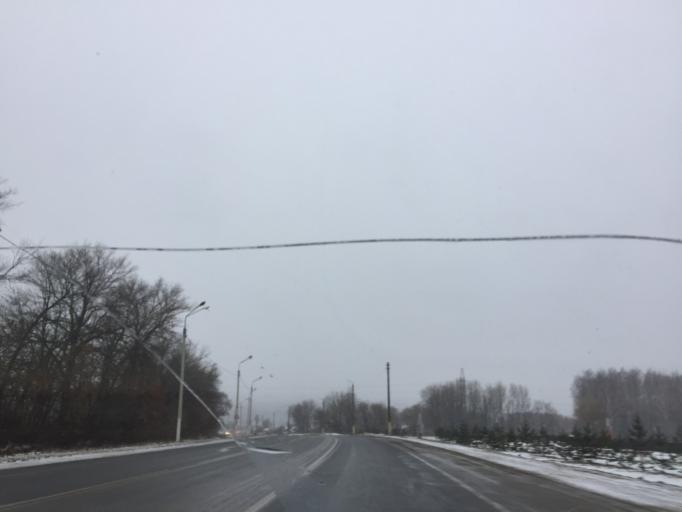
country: RU
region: Tula
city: Plavsk
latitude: 53.7245
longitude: 37.3006
